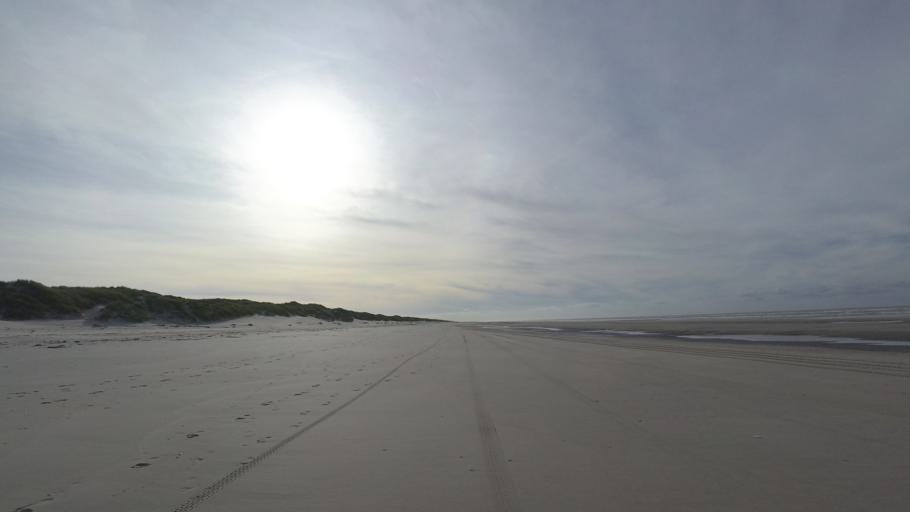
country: NL
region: Friesland
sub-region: Gemeente Dongeradeel
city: Holwerd
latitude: 53.4667
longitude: 5.8882
